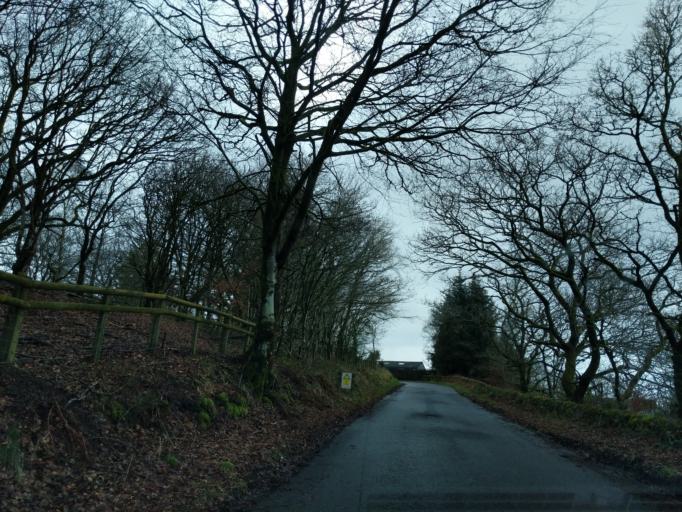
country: GB
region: Scotland
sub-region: Dumfries and Galloway
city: Moffat
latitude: 55.3219
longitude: -3.4296
